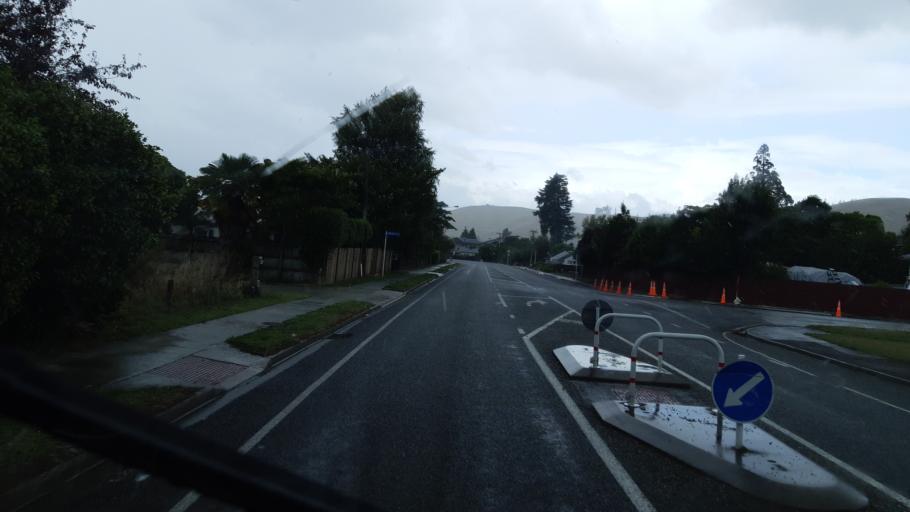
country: NZ
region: Tasman
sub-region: Tasman District
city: Wakefield
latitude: -41.4041
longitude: 173.0474
